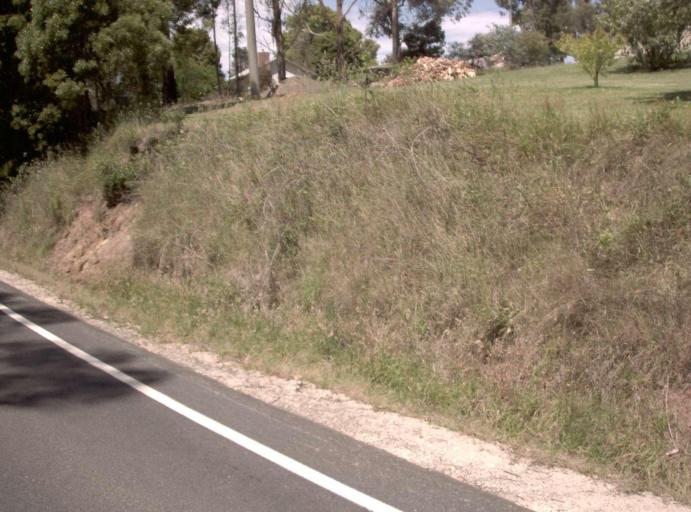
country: AU
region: New South Wales
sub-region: Bombala
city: Bombala
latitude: -37.5645
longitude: 149.1556
